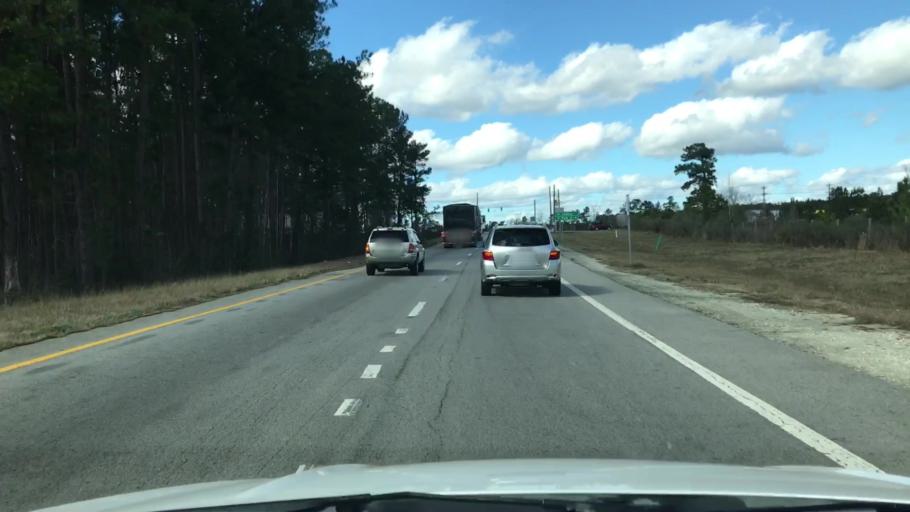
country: US
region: South Carolina
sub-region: Dorchester County
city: Summerville
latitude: 33.0814
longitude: -80.2055
